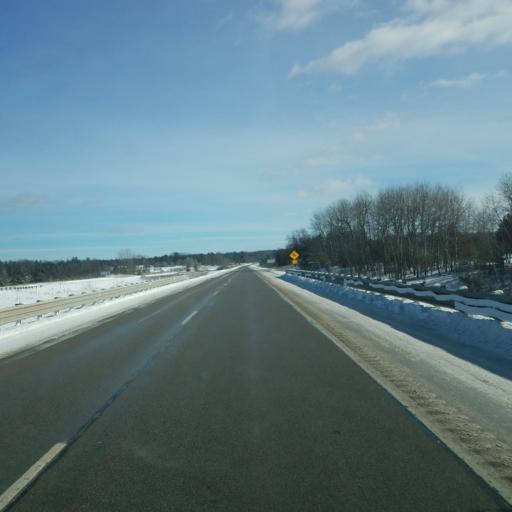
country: US
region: Michigan
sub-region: Clare County
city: Clare
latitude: 43.8677
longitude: -84.8982
